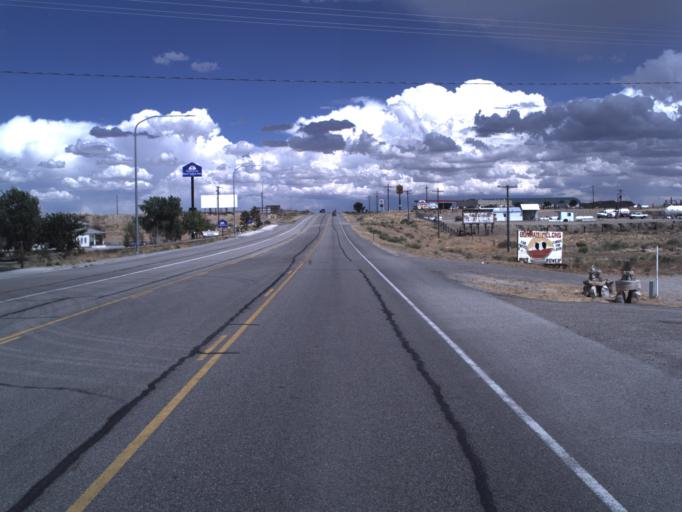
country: US
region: Utah
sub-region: Carbon County
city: East Carbon City
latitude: 38.9927
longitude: -110.1390
